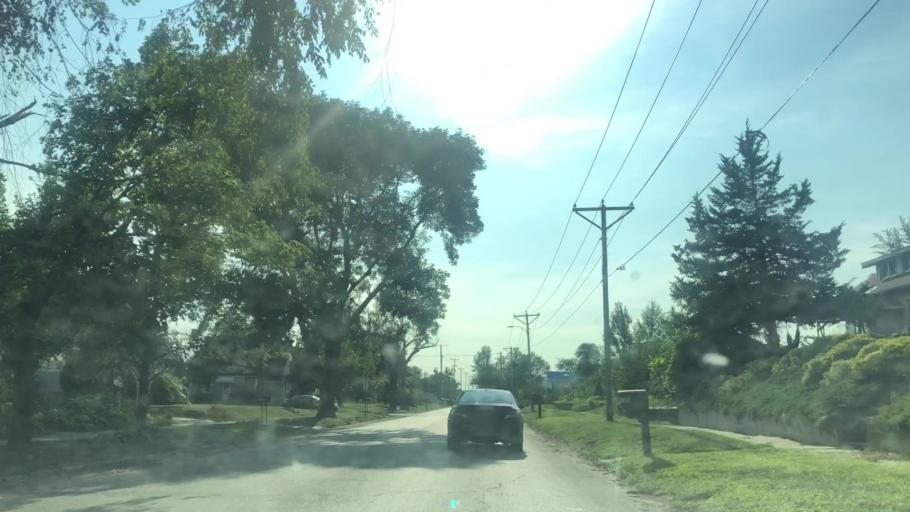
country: US
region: Iowa
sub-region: Marshall County
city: Marshalltown
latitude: 42.0527
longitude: -92.9389
